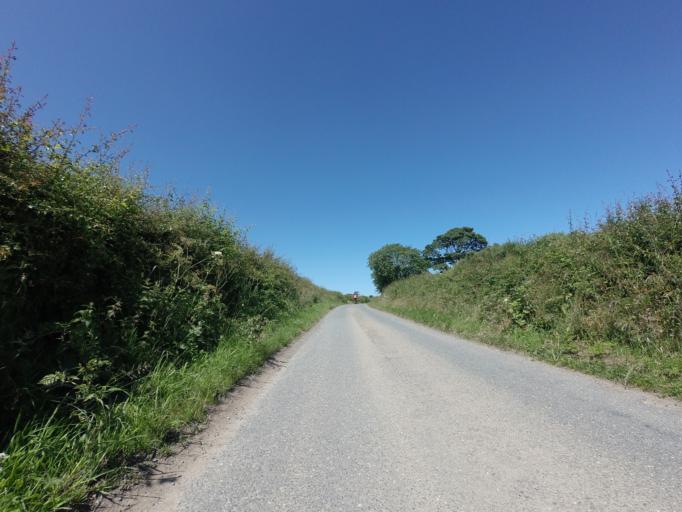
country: GB
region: Scotland
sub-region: Aberdeenshire
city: Macduff
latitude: 57.6344
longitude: -2.4903
